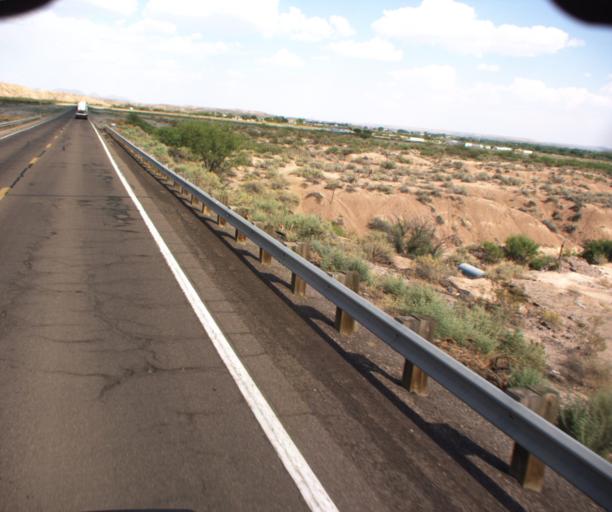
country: US
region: Arizona
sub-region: Greenlee County
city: Clifton
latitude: 32.7524
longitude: -109.1219
